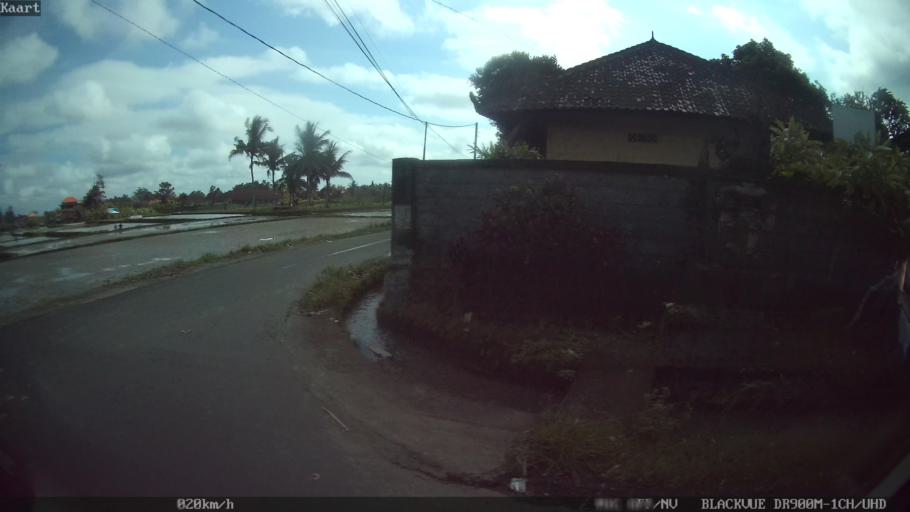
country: ID
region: Bali
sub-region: Kabupaten Gianyar
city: Ubud
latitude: -8.5101
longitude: 115.2822
